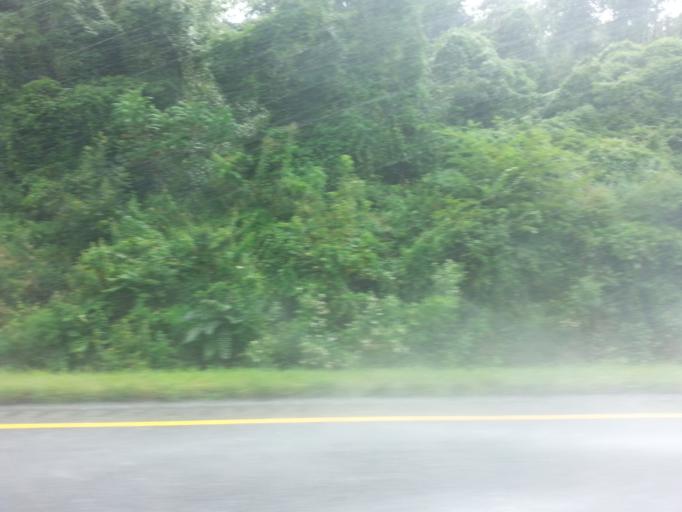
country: US
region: Tennessee
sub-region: Smith County
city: Gordonsville
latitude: 36.1692
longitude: -85.9040
